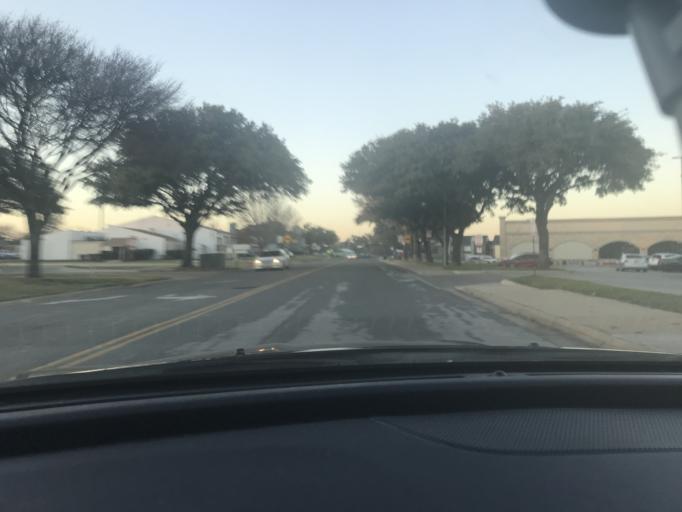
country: US
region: Texas
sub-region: Tarrant County
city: Arlington
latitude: 32.7657
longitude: -97.0993
